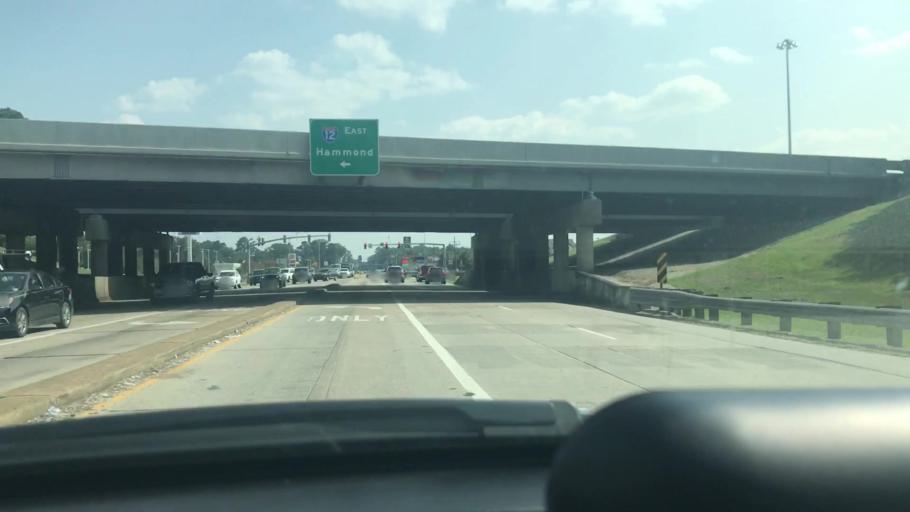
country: US
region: Louisiana
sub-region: Livingston Parish
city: Denham Springs
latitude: 30.4555
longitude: -90.9566
